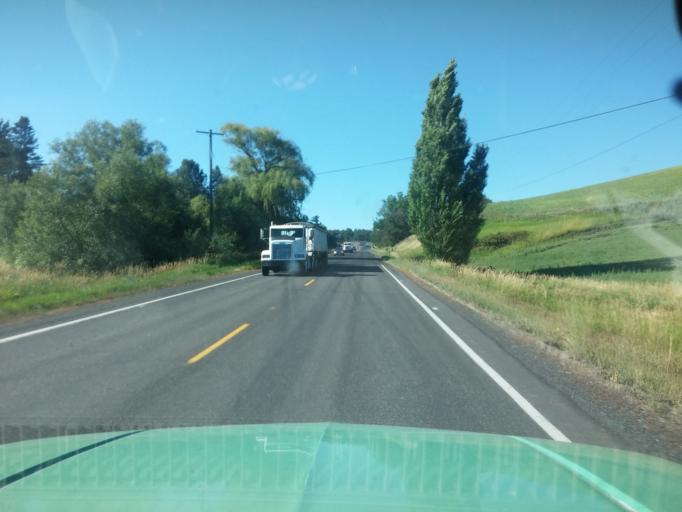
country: US
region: Idaho
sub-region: Latah County
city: Moscow
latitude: 46.7019
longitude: -117.0067
